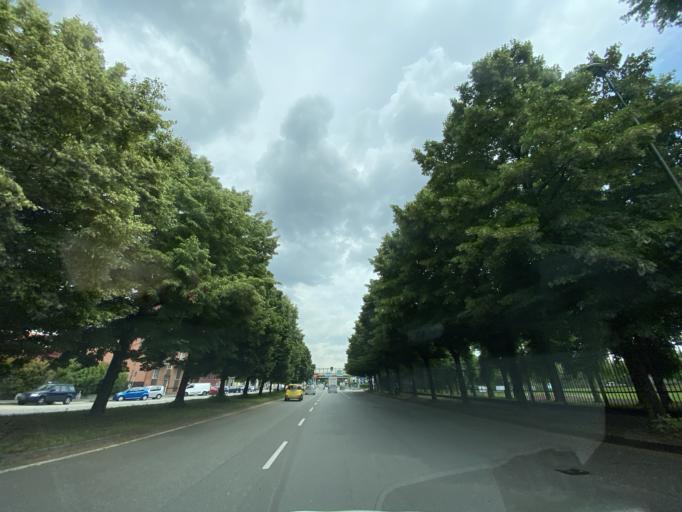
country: IT
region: Lombardy
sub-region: Citta metropolitana di Milano
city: Cologno Monzese
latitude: 45.5266
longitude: 9.2561
